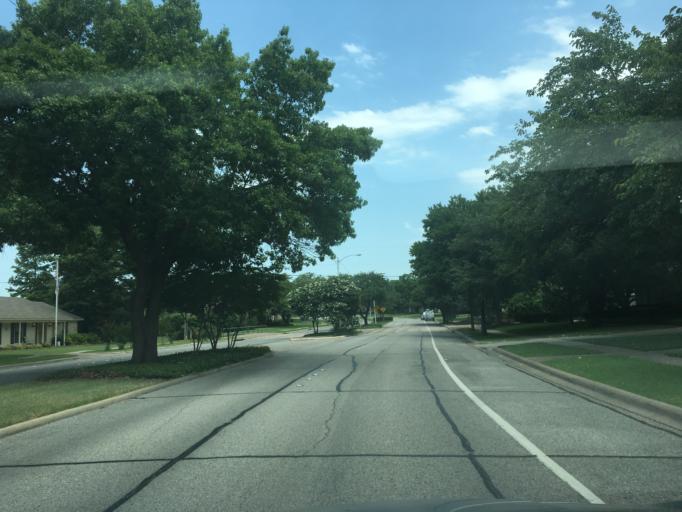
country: US
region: Texas
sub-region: Dallas County
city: Carrollton
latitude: 32.9371
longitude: -96.8697
